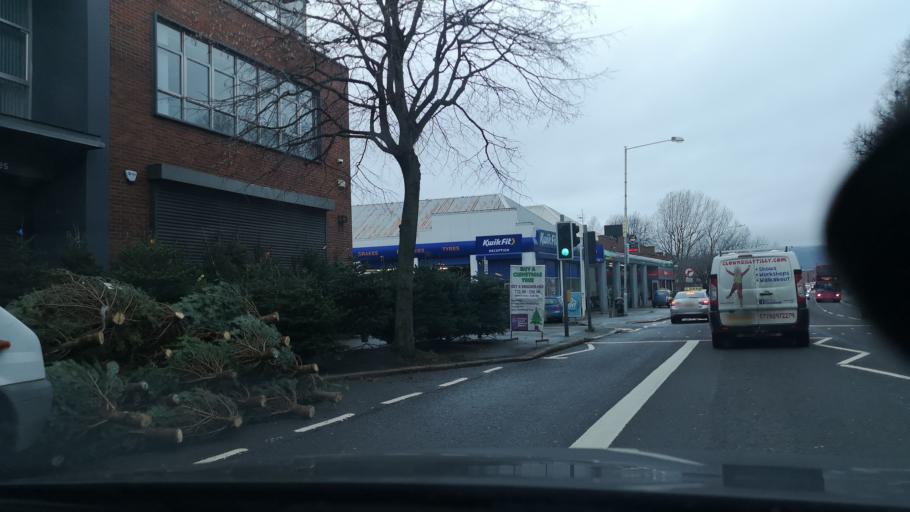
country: GB
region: Northern Ireland
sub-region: City of Belfast
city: Belfast
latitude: 54.5811
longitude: -5.9212
